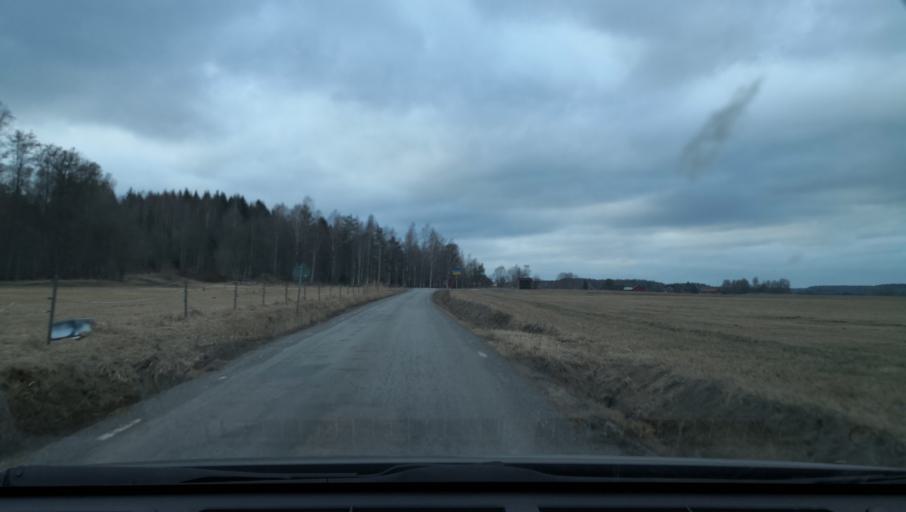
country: SE
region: Vaestmanland
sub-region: Kopings Kommun
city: Kolsva
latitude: 59.5568
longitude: 15.8714
